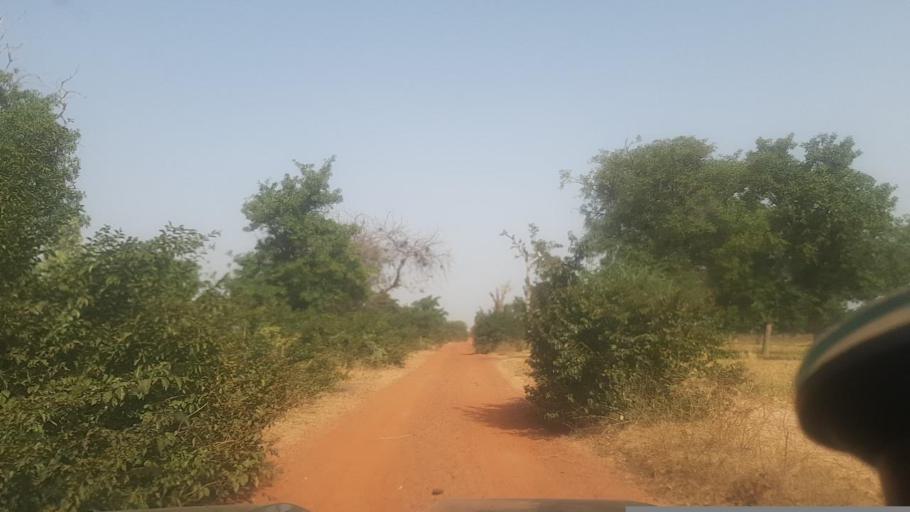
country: ML
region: Segou
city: Bla
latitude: 12.8515
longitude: -5.9845
